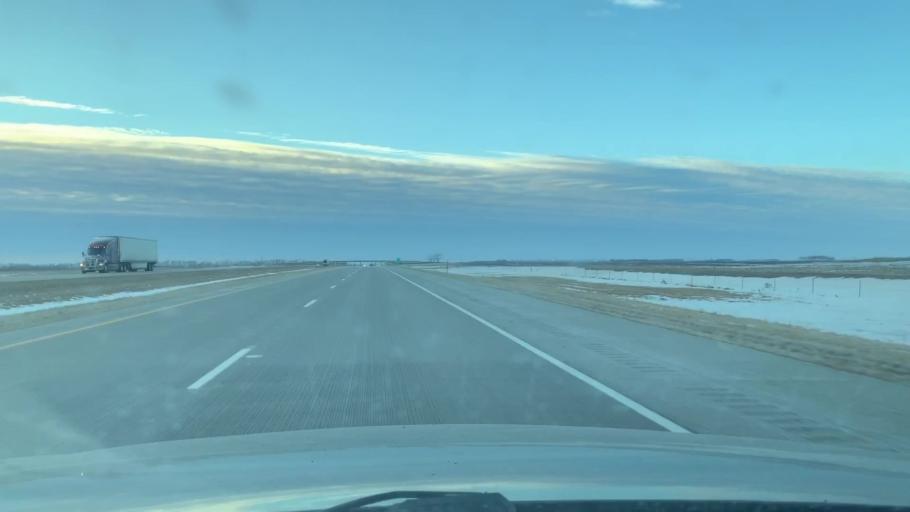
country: US
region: North Dakota
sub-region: Cass County
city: Casselton
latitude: 46.8758
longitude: -97.4788
